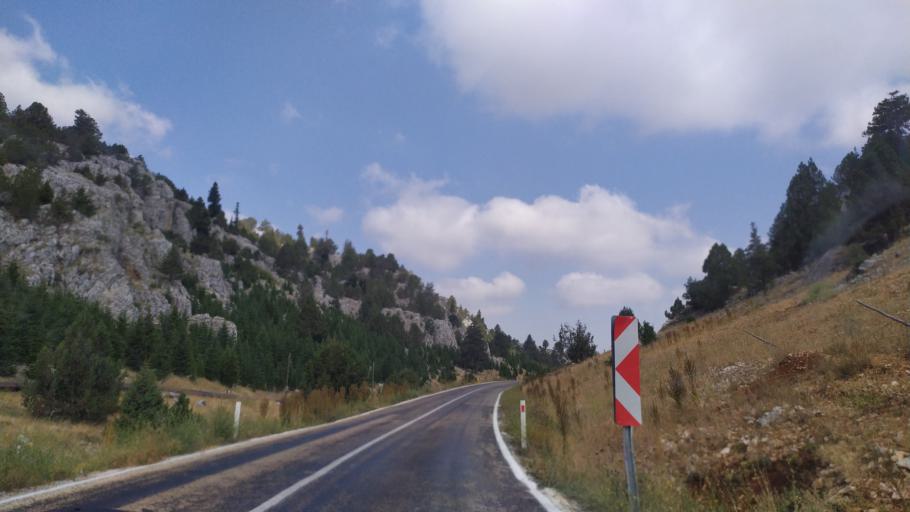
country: TR
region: Mersin
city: Kirobasi
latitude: 36.6162
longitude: 33.8755
